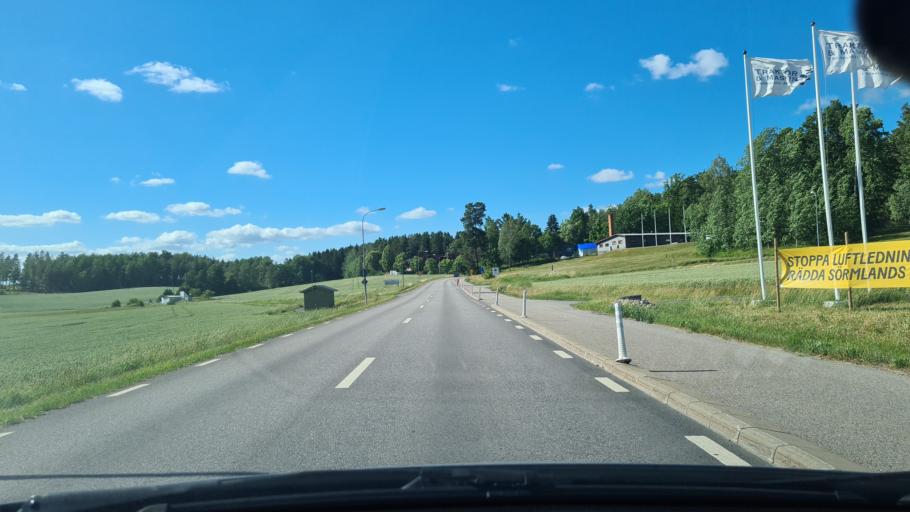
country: SE
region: Soedermanland
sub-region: Nykopings Kommun
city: Olstorp
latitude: 58.8317
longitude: 16.5173
